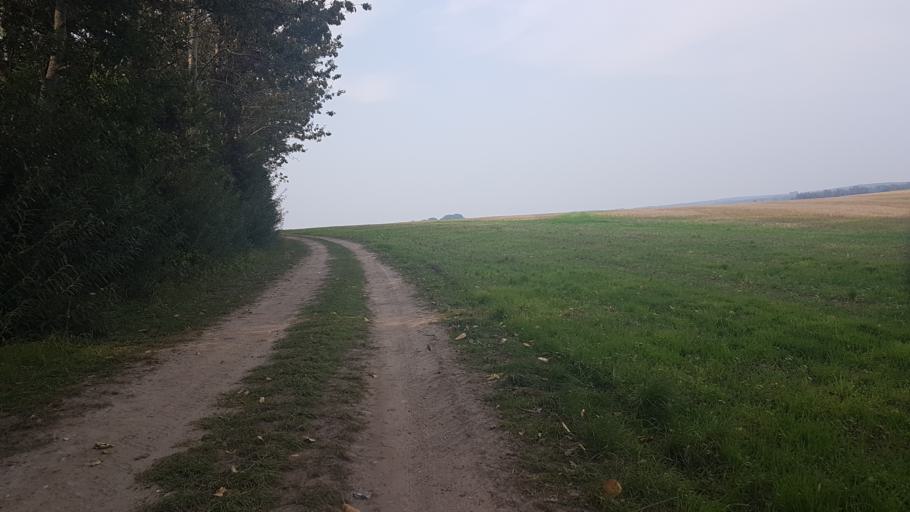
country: DE
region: Mecklenburg-Vorpommern
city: Garz
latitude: 54.2977
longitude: 13.3636
